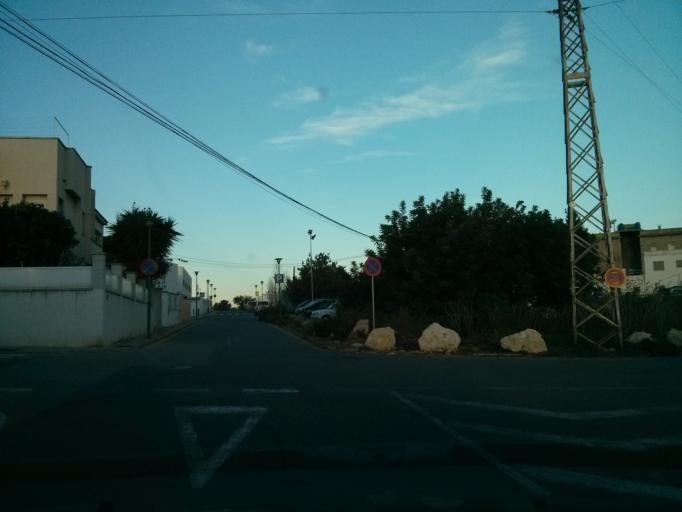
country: ES
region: Catalonia
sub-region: Provincia de Tarragona
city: El Vendrell
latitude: 41.1869
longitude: 1.5237
